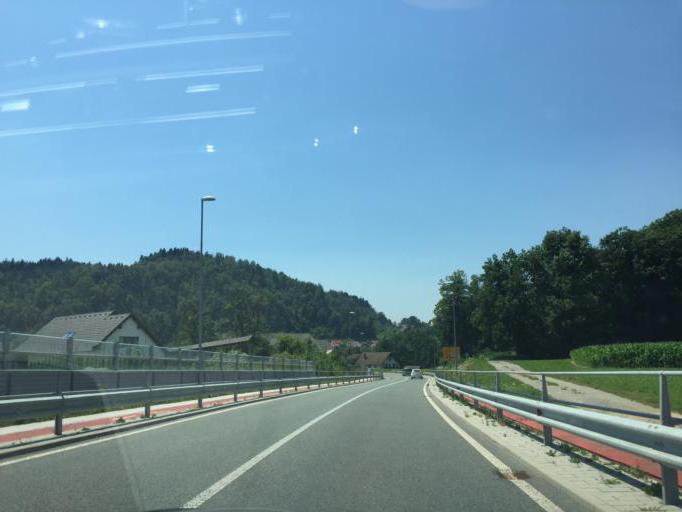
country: SI
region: Skofja Loka
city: Skofja Loka
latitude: 46.1664
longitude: 14.3244
